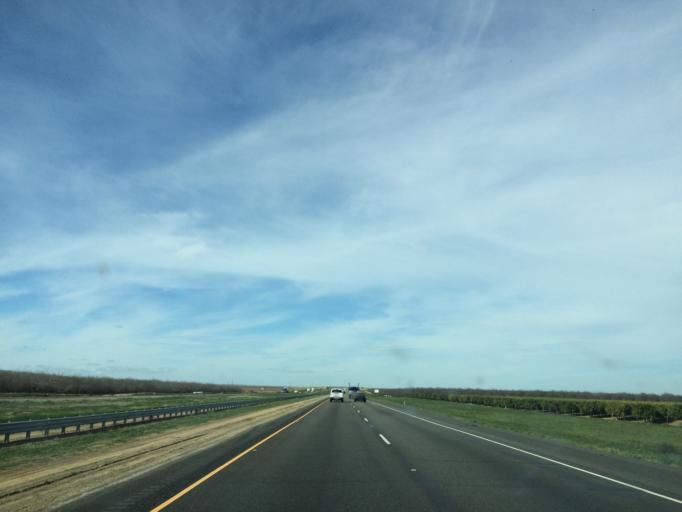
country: US
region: California
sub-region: Merced County
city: South Dos Palos
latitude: 36.7100
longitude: -120.6767
